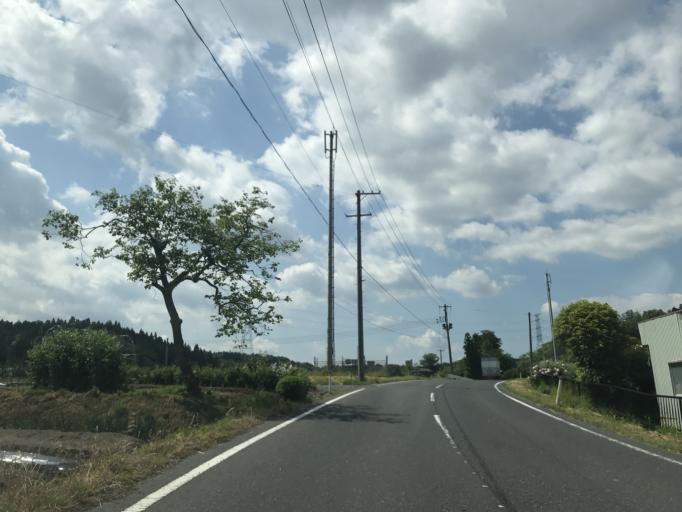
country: JP
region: Miyagi
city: Furukawa
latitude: 38.7846
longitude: 140.9581
